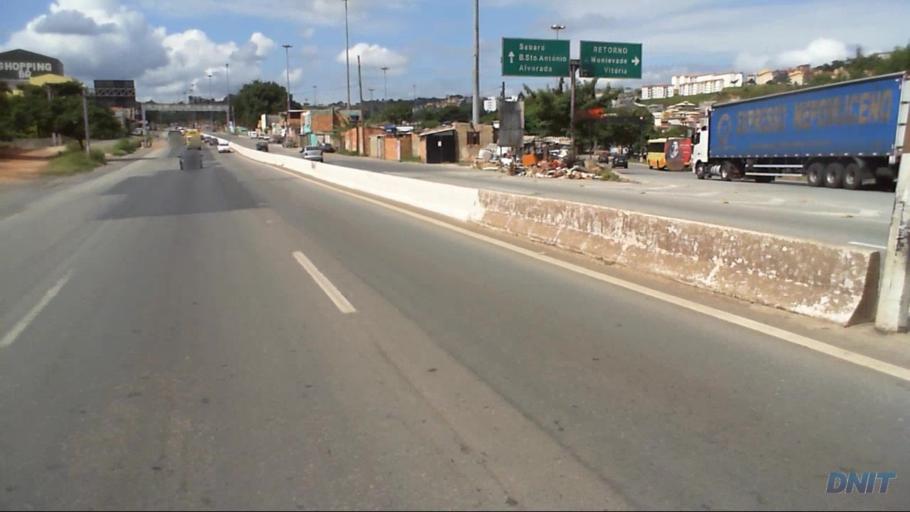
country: BR
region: Minas Gerais
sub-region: Belo Horizonte
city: Belo Horizonte
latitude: -19.8565
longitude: -43.8991
